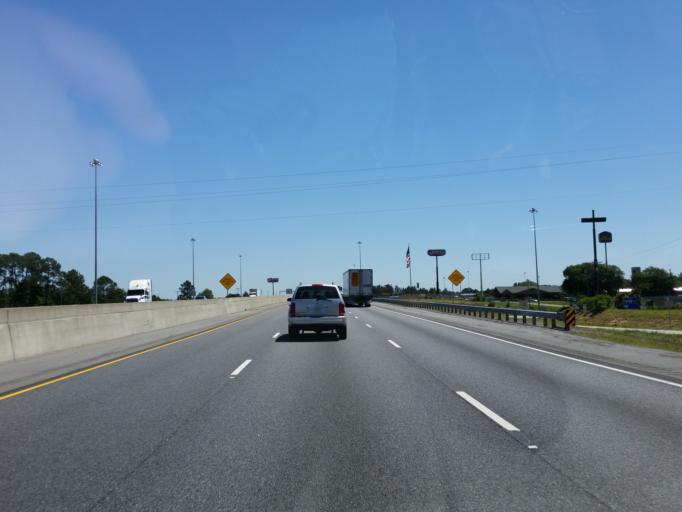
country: US
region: Georgia
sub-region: Turner County
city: Ashburn
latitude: 31.7135
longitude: -83.6380
